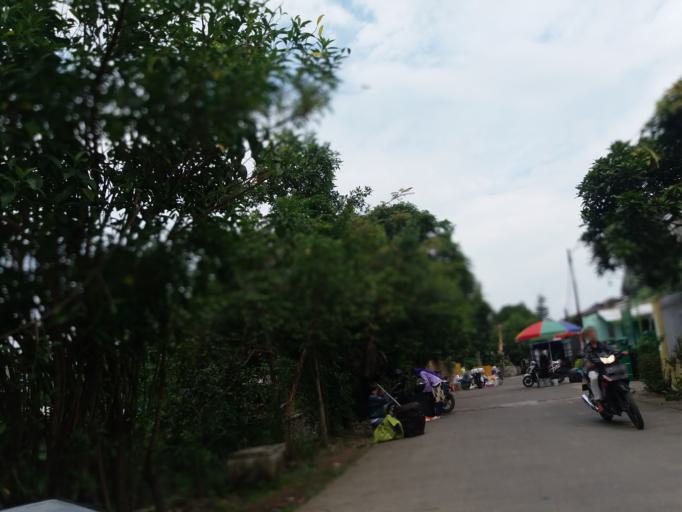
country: ID
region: West Java
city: Bandung
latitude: -6.9233
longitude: 107.6495
